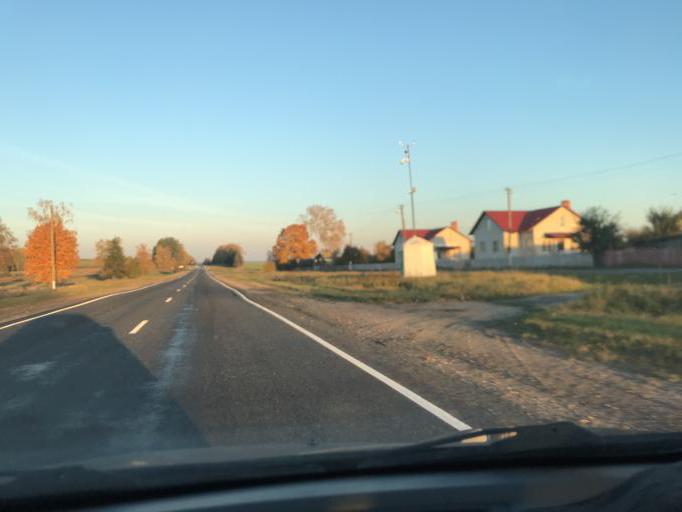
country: BY
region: Minsk
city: Staryya Darohi
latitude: 53.0600
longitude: 28.4787
